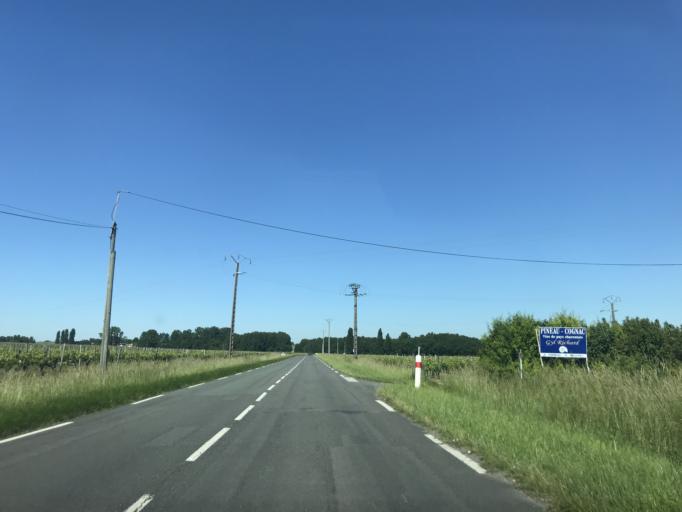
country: FR
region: Poitou-Charentes
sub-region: Departement de la Charente-Maritime
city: Perignac
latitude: 45.5755
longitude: -0.4728
